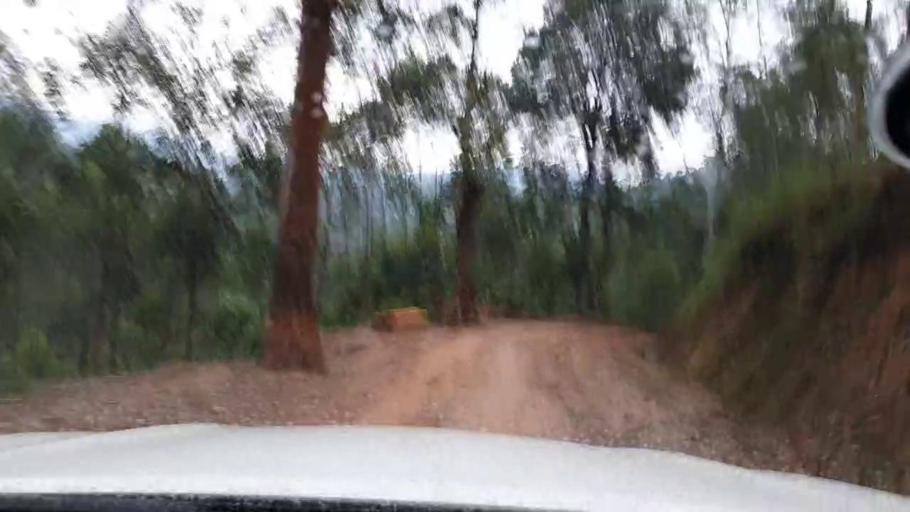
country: RW
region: Western Province
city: Cyangugu
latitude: -2.4125
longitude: 29.1980
